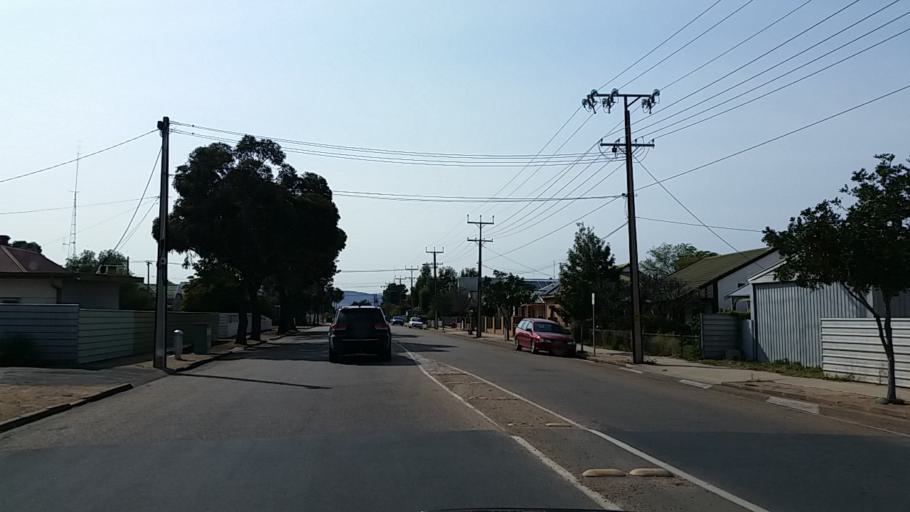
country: AU
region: South Australia
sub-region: Port Pirie City and Dists
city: Port Pirie
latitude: -33.1893
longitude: 137.9977
